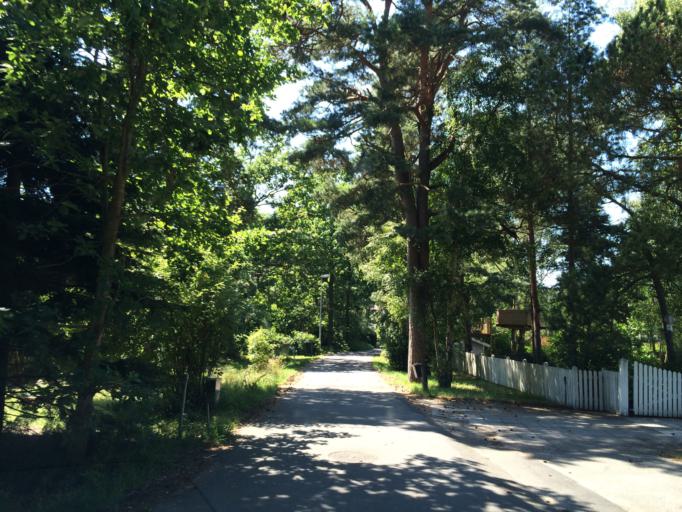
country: SE
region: Skane
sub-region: Vellinge Kommun
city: Ljunghusen
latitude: 55.4081
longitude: 12.9341
